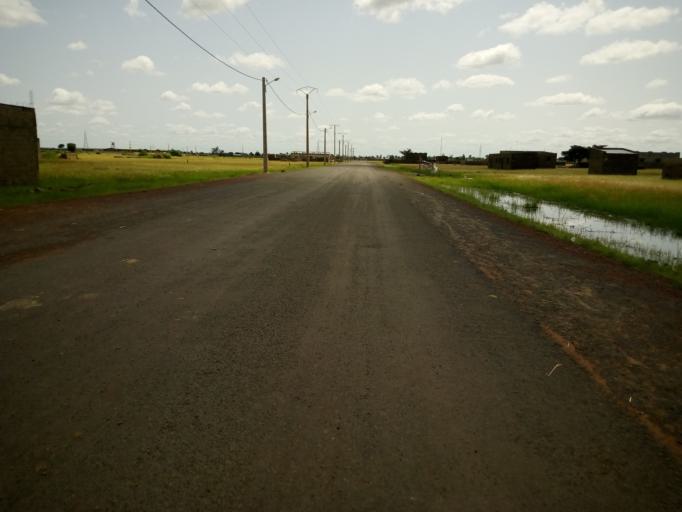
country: ML
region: Segou
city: Segou
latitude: 13.4144
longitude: -6.2213
